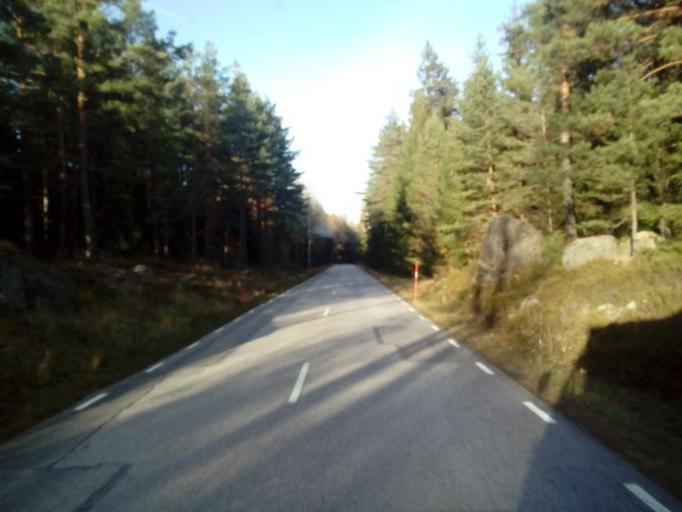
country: SE
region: Kalmar
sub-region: Vasterviks Kommun
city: Ankarsrum
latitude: 57.7470
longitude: 16.1130
